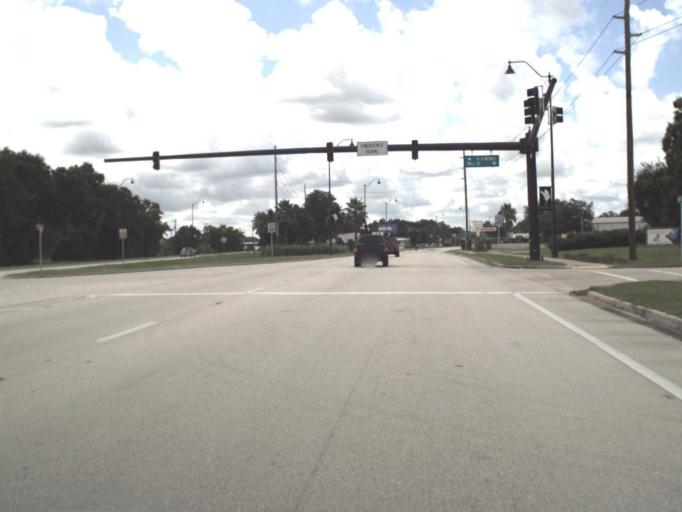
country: US
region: Florida
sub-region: Hardee County
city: Wauchula
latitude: 27.5578
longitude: -81.8133
